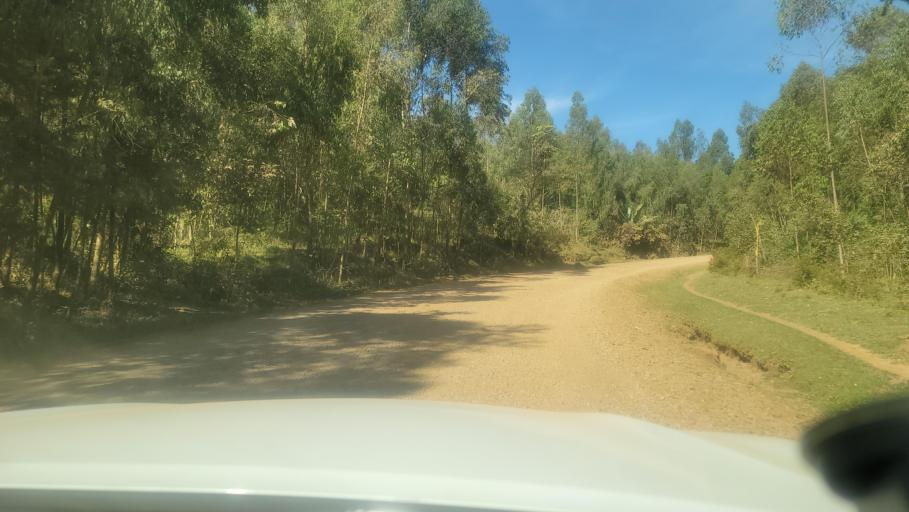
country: ET
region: Oromiya
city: Agaro
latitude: 7.8002
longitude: 36.4672
